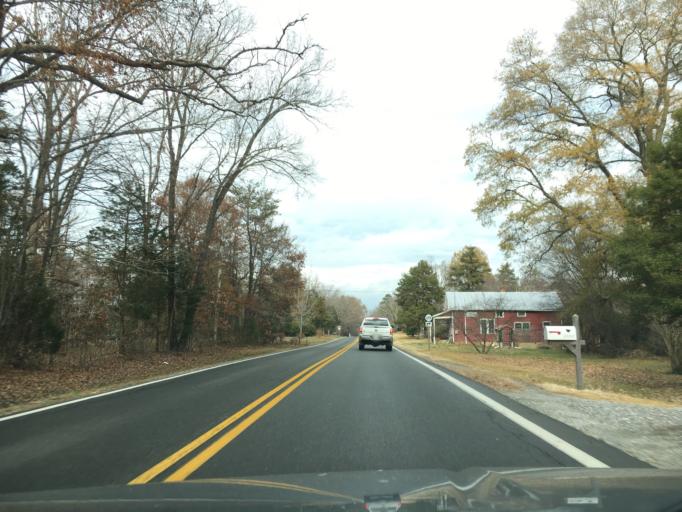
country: US
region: Virginia
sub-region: Prince Edward County
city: Farmville
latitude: 37.3850
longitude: -78.3723
